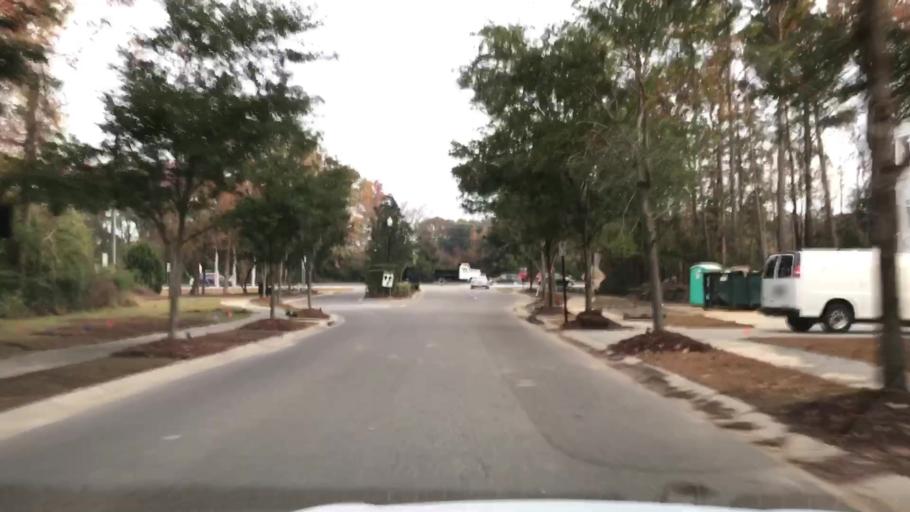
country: US
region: South Carolina
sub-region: Charleston County
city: Shell Point
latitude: 32.8104
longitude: -80.0515
